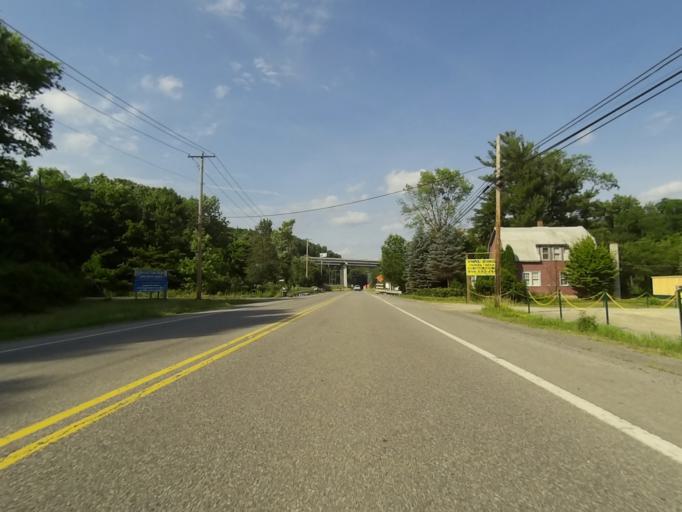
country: US
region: Pennsylvania
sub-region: Centre County
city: Stormstown
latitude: 40.8081
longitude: -78.0451
